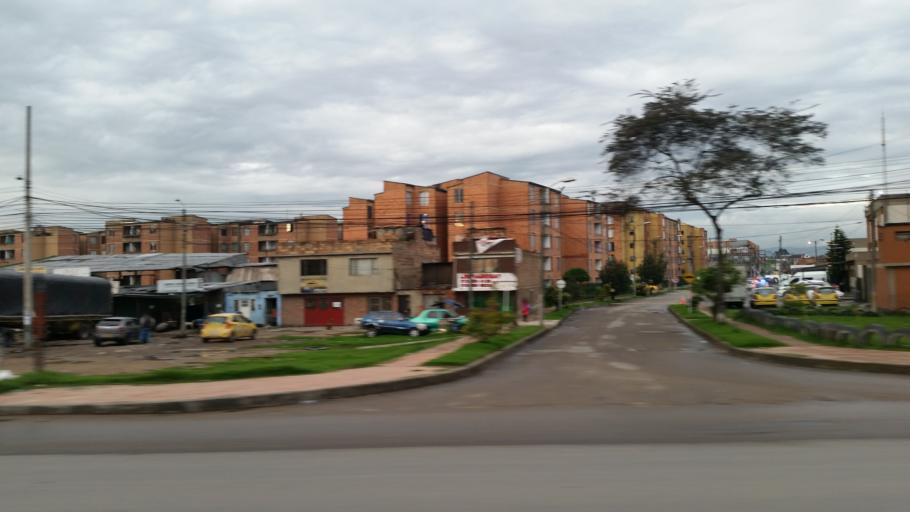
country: CO
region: Cundinamarca
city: Funza
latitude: 4.6671
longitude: -74.1494
